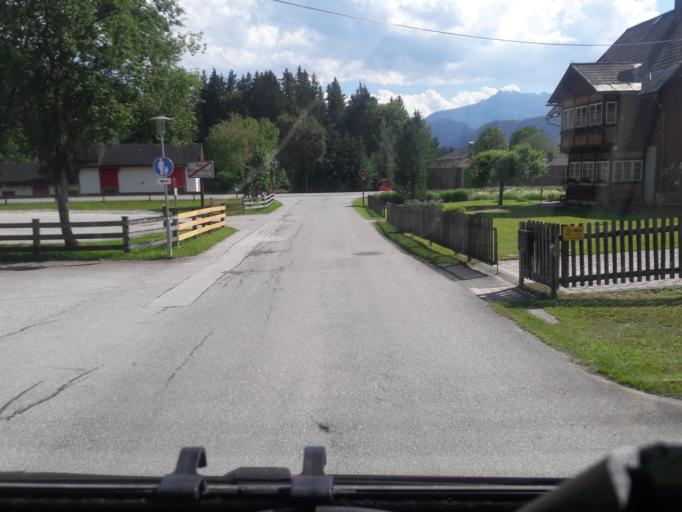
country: AT
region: Styria
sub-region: Politischer Bezirk Liezen
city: Tauplitz
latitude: 47.5526
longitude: 13.9504
